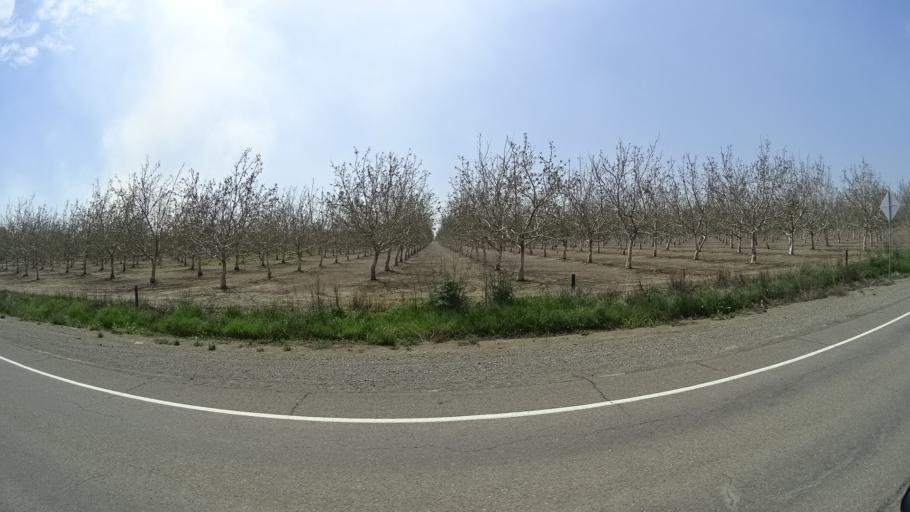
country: US
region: California
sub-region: Butte County
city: Biggs
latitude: 39.4641
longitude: -121.9269
